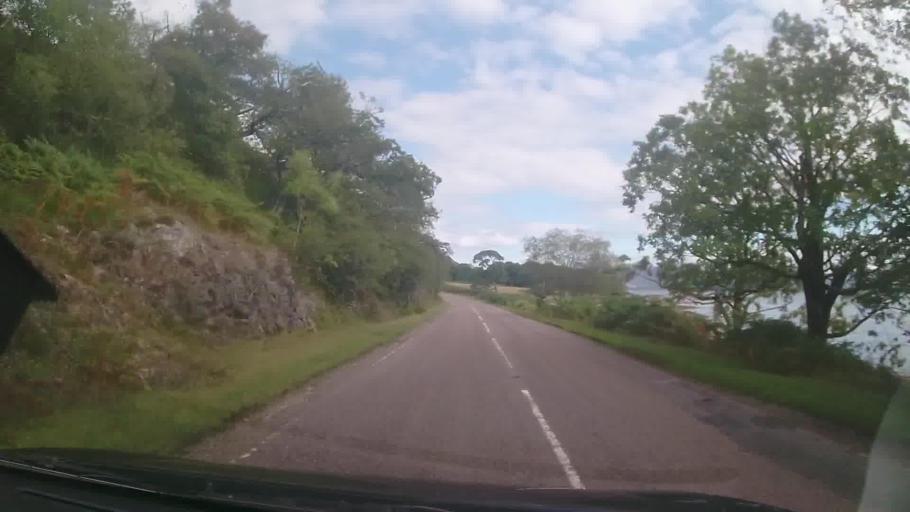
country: GB
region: Scotland
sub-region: Highland
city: Fort William
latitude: 56.6919
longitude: -5.3387
